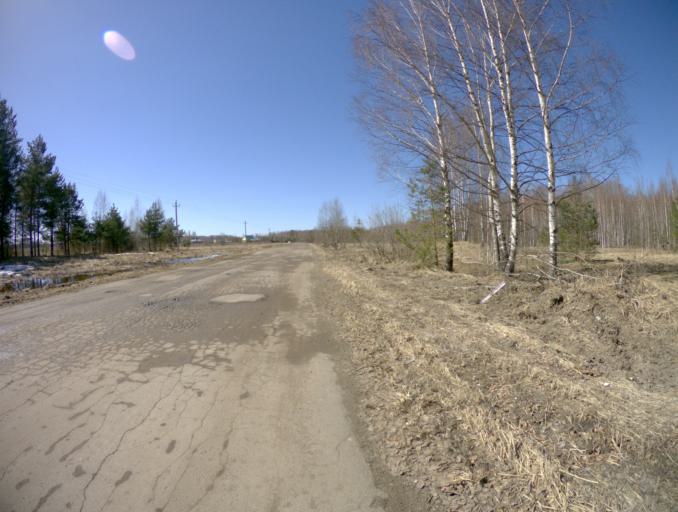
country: RU
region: Vladimir
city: Orgtrud
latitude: 56.2810
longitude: 40.7113
